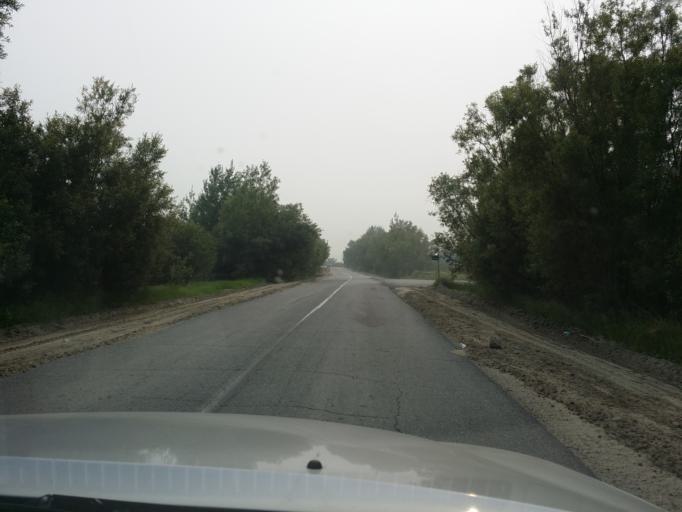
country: RU
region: Khanty-Mansiyskiy Avtonomnyy Okrug
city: Megion
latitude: 60.9747
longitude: 76.2957
